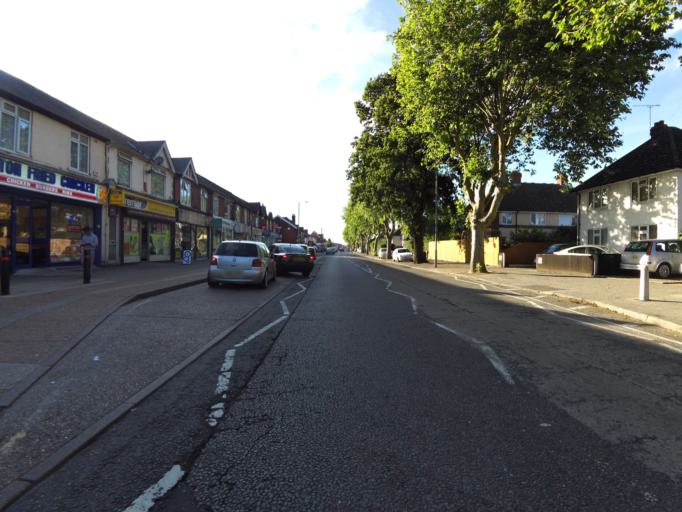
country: GB
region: England
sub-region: Suffolk
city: Ipswich
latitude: 52.0388
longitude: 1.1874
